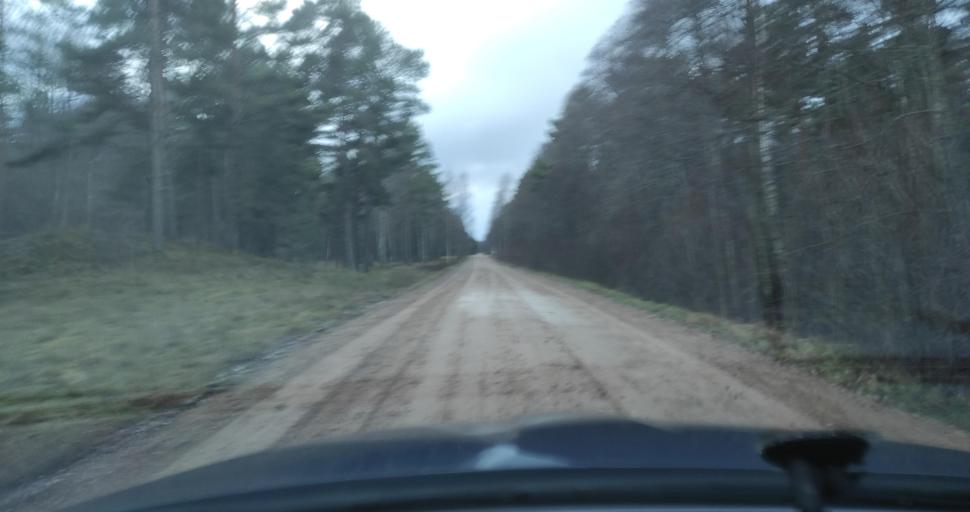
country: LV
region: Pavilostas
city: Pavilosta
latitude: 56.8534
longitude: 21.1191
